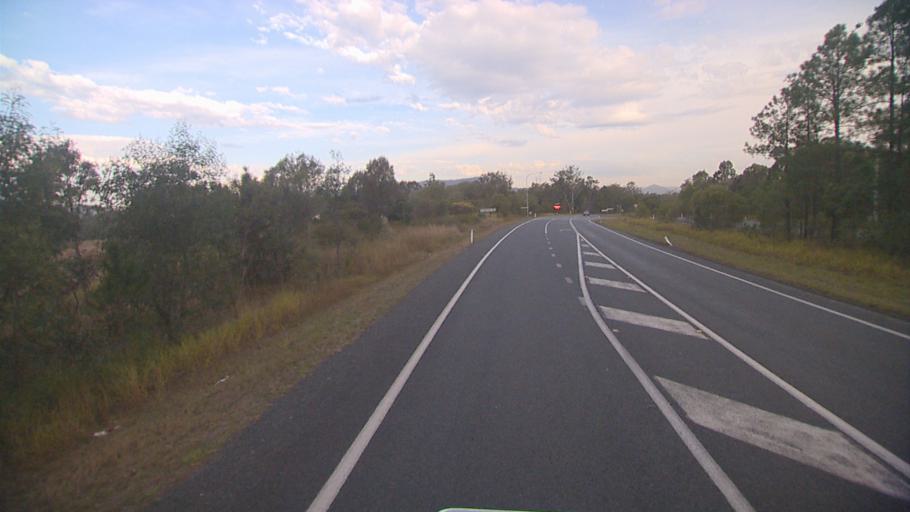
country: AU
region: Queensland
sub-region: Logan
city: Cedar Vale
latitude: -27.8486
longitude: 153.1209
